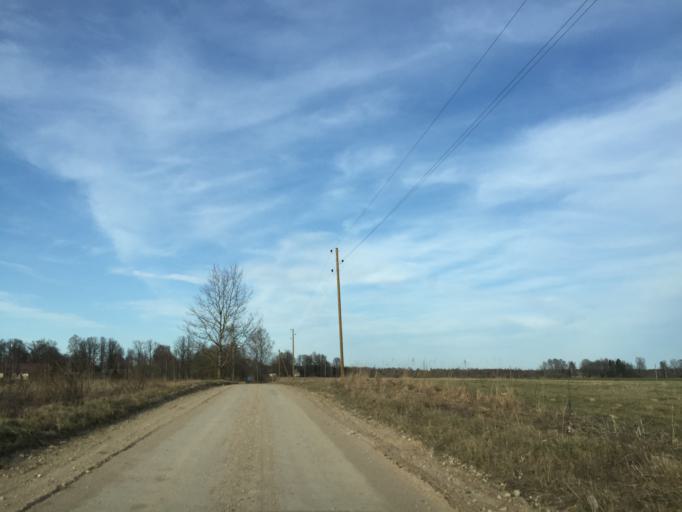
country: LV
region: Kegums
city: Kegums
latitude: 56.8036
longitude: 24.7748
